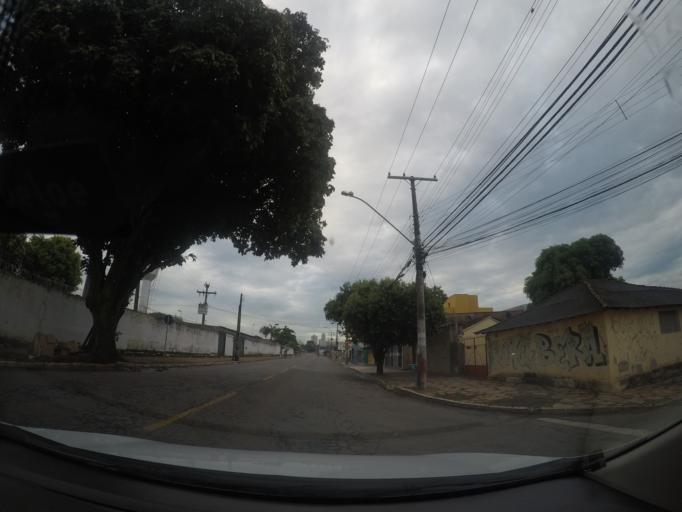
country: BR
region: Goias
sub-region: Goiania
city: Goiania
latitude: -16.6585
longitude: -49.2524
